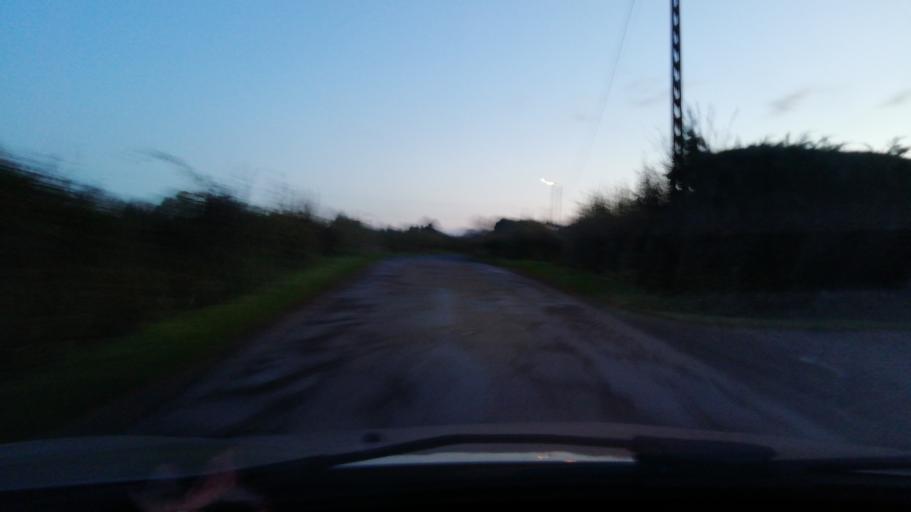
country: FR
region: Nord-Pas-de-Calais
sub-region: Departement du Nord
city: Marpent
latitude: 50.2630
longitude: 4.0850
